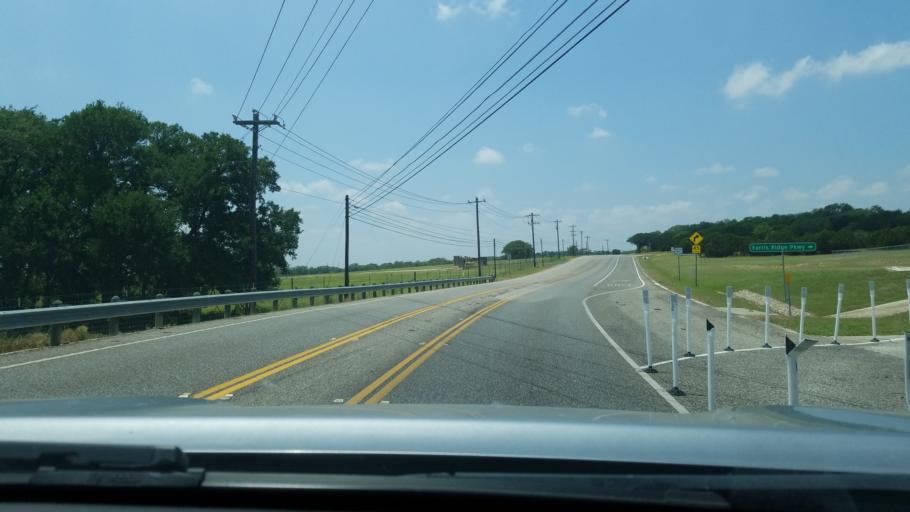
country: US
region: Texas
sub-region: Hays County
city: Woodcreek
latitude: 30.0180
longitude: -98.1431
